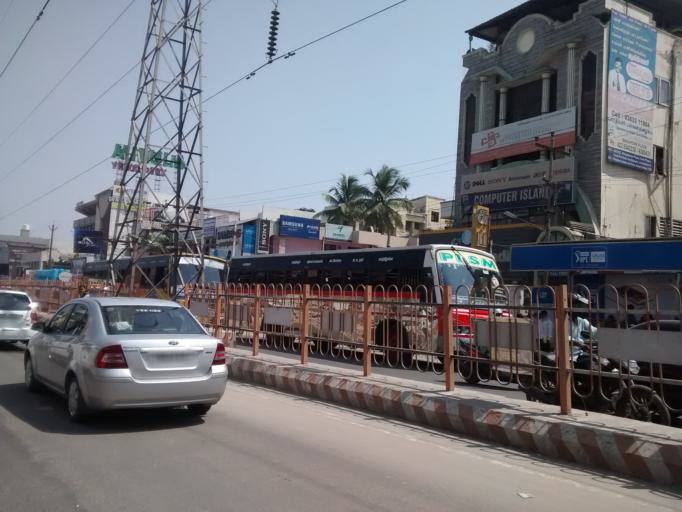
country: IN
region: Tamil Nadu
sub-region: Coimbatore
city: Coimbatore
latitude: 11.0193
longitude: 76.9625
